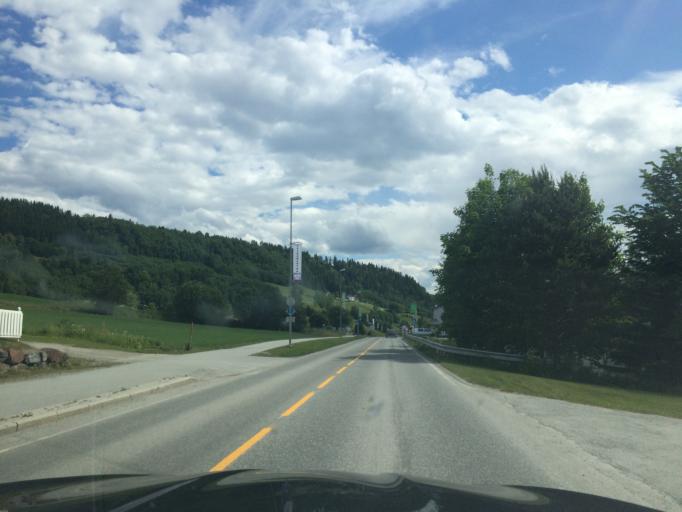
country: NO
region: Sor-Trondelag
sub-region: Selbu
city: Mebonden
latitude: 63.2205
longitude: 11.0389
